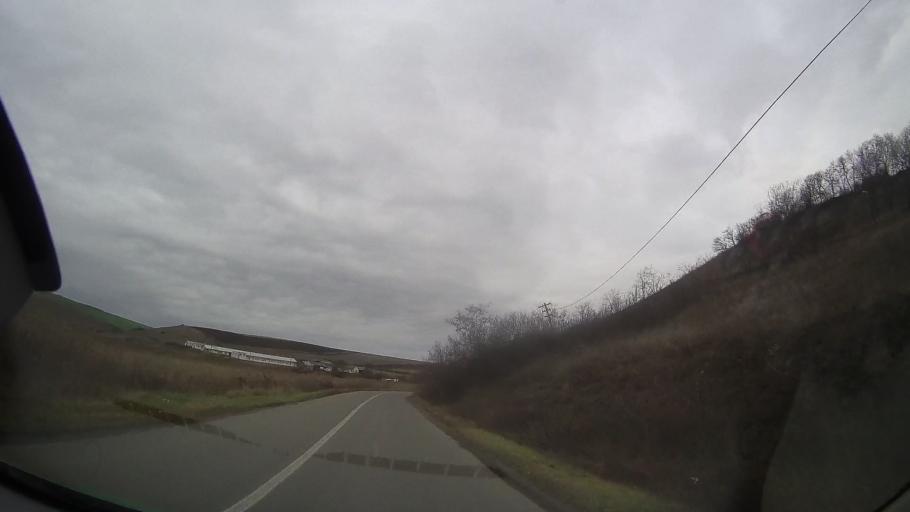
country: RO
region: Mures
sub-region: Comuna Faragau
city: Faragau
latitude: 46.7539
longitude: 24.5216
